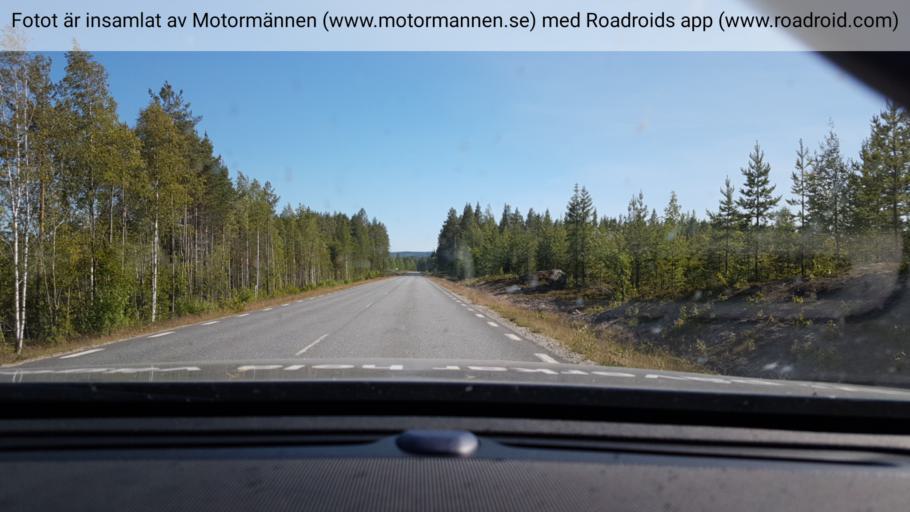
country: SE
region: Vaesterbotten
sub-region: Lycksele Kommun
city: Lycksele
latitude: 64.4958
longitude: 18.8976
